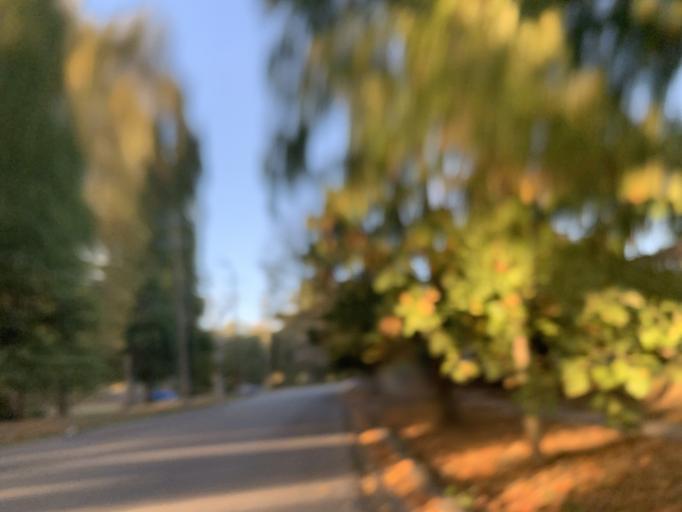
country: US
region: Indiana
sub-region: Floyd County
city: New Albany
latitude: 38.2556
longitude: -85.8262
